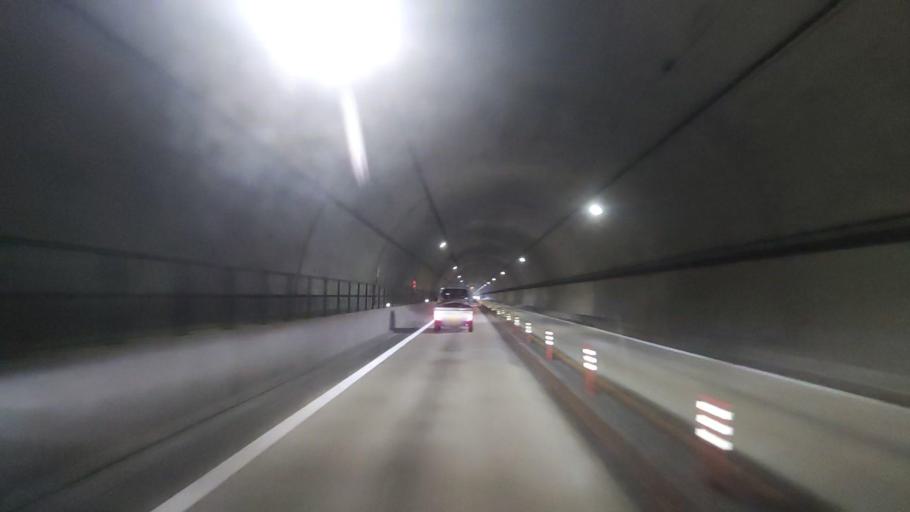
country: JP
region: Wakayama
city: Tanabe
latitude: 33.6243
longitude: 135.4179
